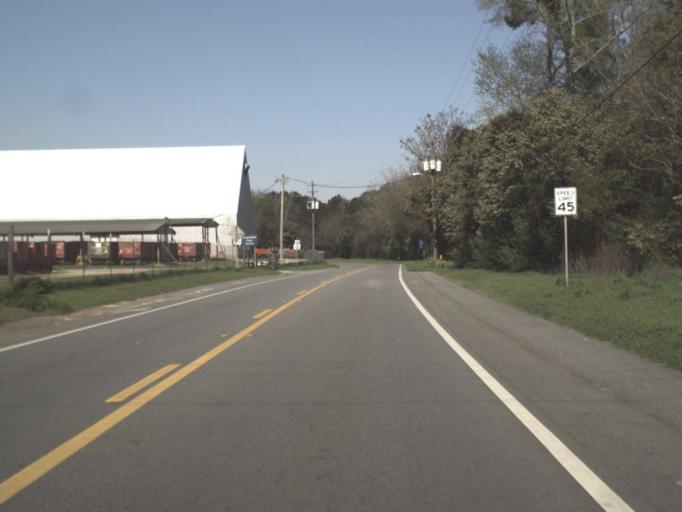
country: US
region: Florida
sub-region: Jackson County
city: Graceville
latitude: 30.9507
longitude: -85.4039
